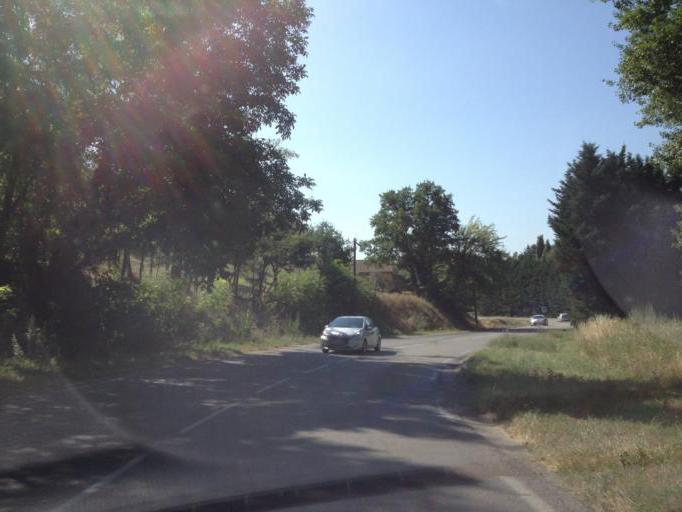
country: FR
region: Rhone-Alpes
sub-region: Departement de la Drome
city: Clerieux
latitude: 45.1204
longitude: 4.9646
